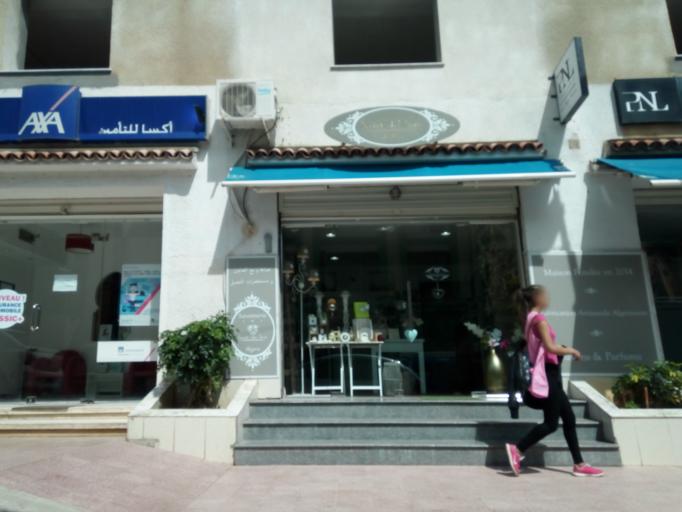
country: DZ
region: Tipaza
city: Douera
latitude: 36.6992
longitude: 2.9708
